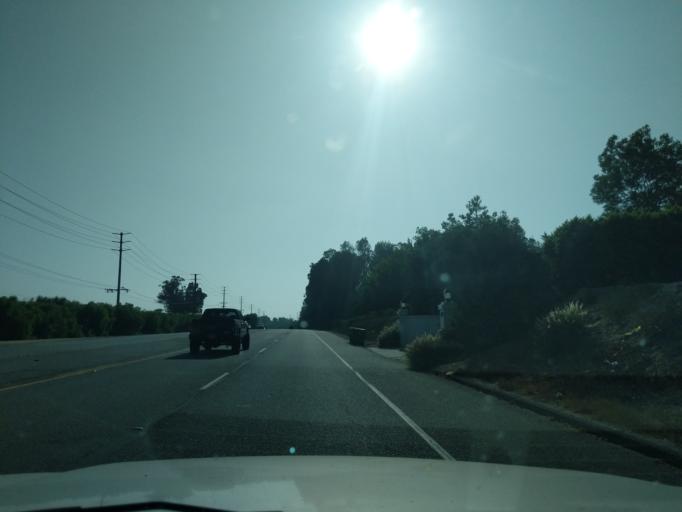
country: US
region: California
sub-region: Ventura County
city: Simi Valley
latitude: 34.2709
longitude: -118.8288
